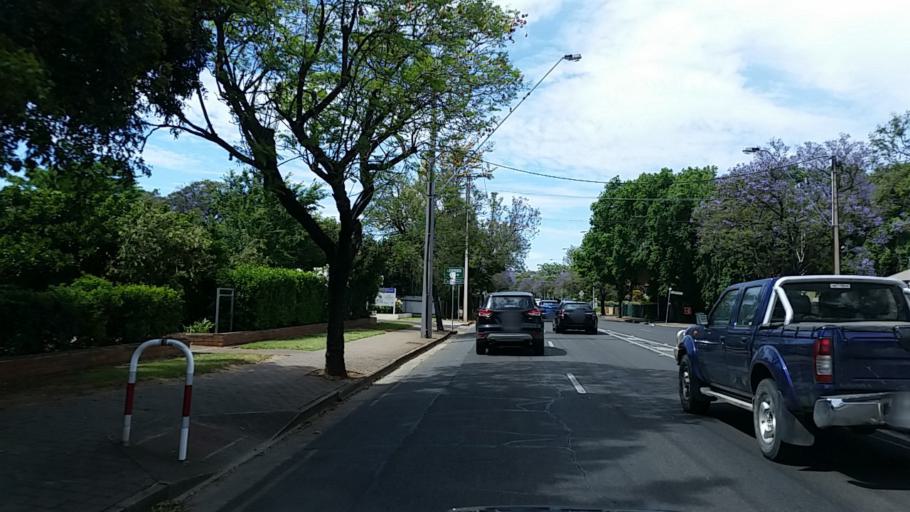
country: AU
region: South Australia
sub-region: Unley
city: Fullarton
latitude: -34.9518
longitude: 138.6255
